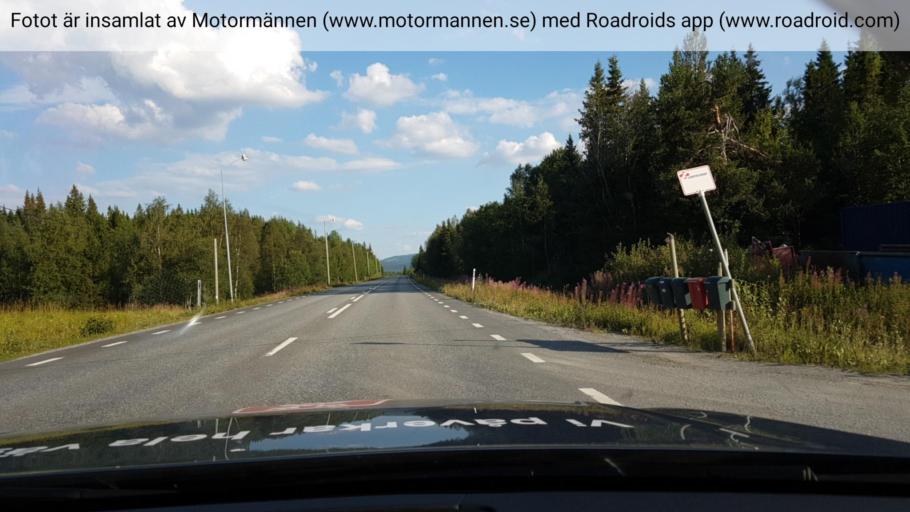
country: SE
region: Jaemtland
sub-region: Are Kommun
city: Are
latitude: 63.3374
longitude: 13.2106
